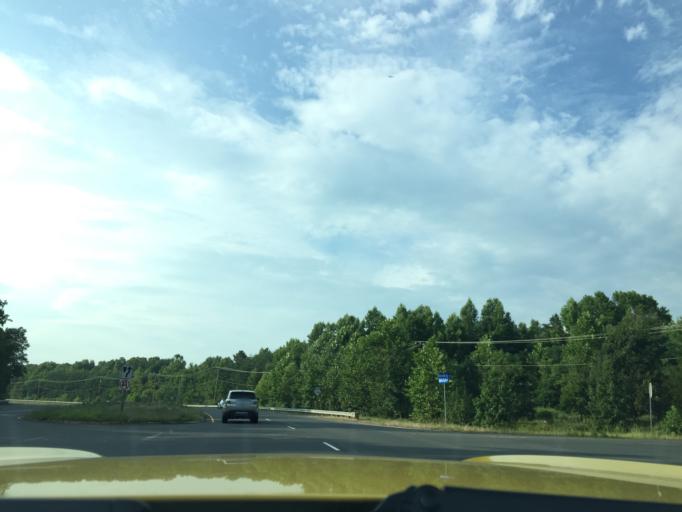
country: US
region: Virginia
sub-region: Fairfax County
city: Fort Belvoir
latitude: 38.7147
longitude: -77.1639
